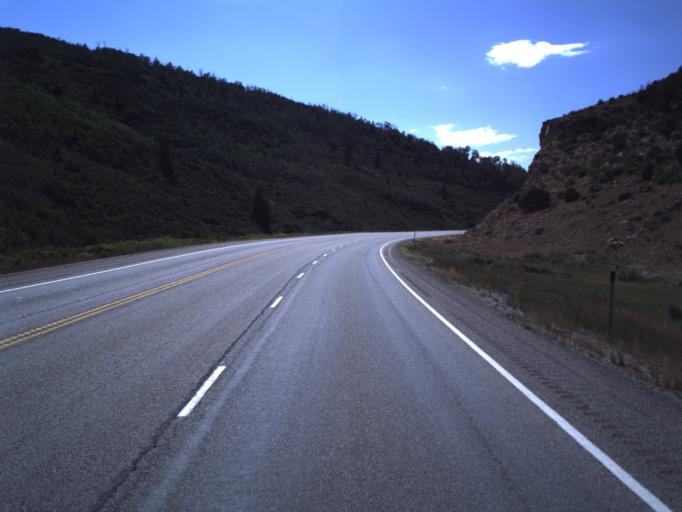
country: US
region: Utah
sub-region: Carbon County
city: Helper
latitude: 40.1924
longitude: -110.9551
